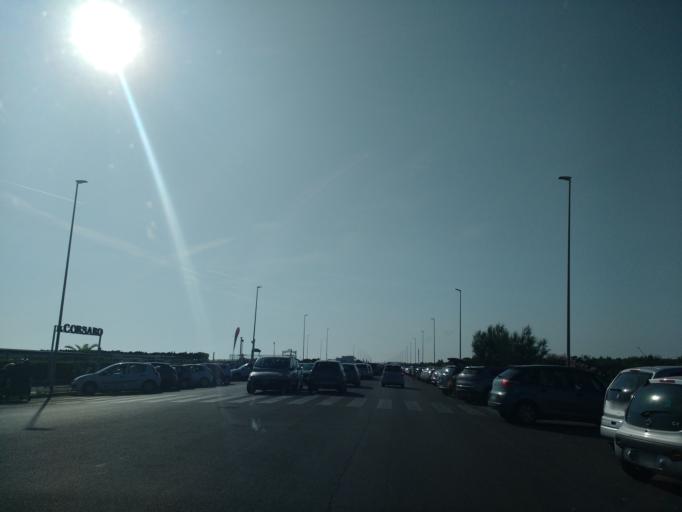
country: IT
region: Latium
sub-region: Citta metropolitana di Roma Capitale
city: Acilia-Castel Fusano-Ostia Antica
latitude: 41.7032
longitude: 12.3430
